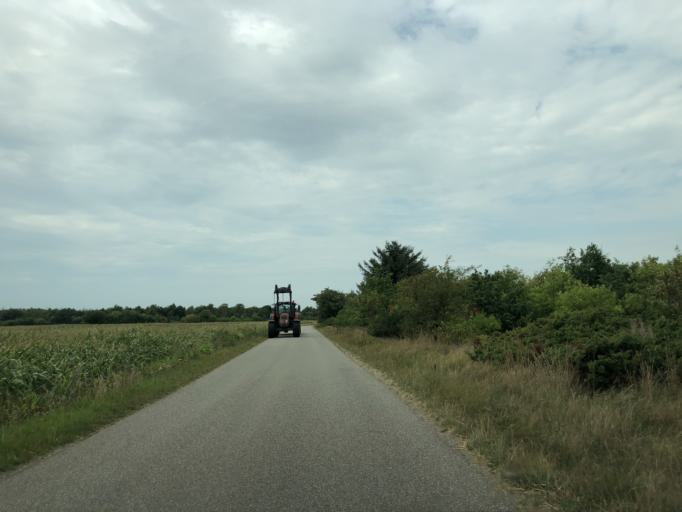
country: DK
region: Central Jutland
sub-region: Holstebro Kommune
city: Ulfborg
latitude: 56.1762
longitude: 8.3259
